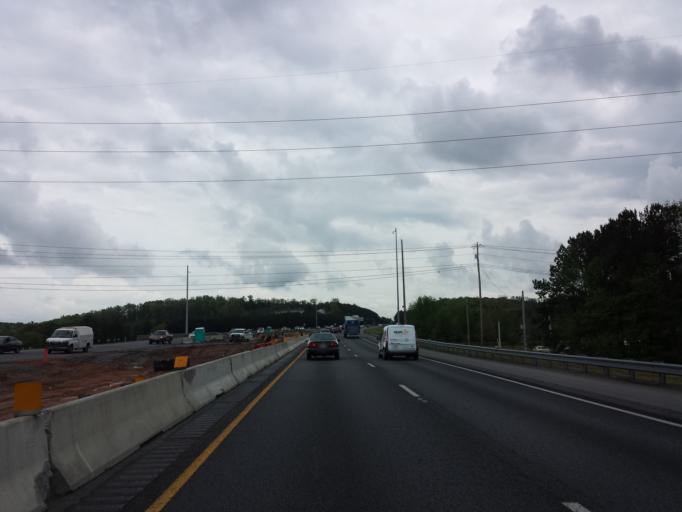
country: US
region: Georgia
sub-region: Cobb County
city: Kennesaw
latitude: 34.0153
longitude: -84.5589
